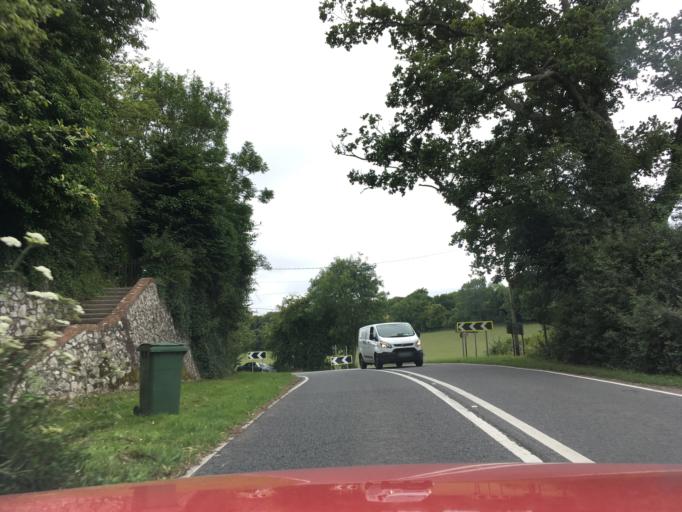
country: GB
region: England
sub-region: Hampshire
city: Petersfield
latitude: 51.0102
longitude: -0.9883
